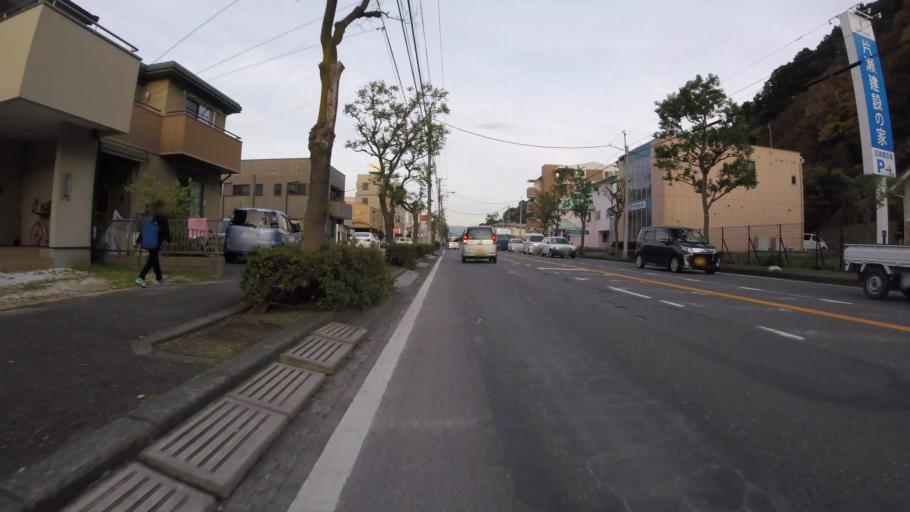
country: JP
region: Shizuoka
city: Numazu
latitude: 35.0986
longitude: 138.8765
